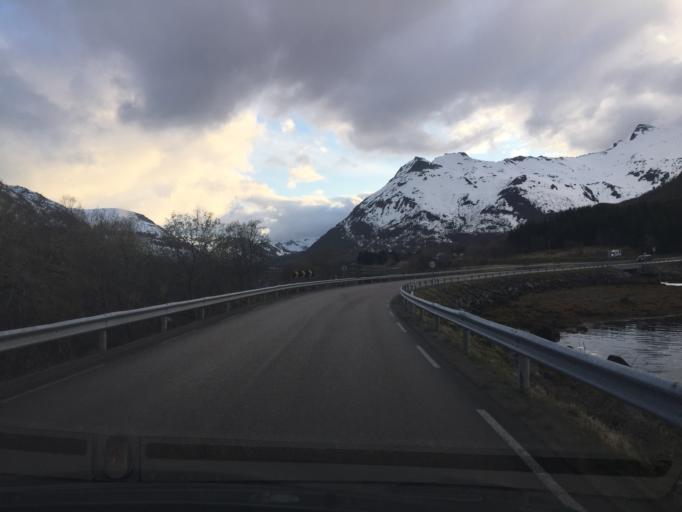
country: NO
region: Nordland
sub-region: Vagan
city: Svolvaer
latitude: 68.3243
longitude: 14.6921
